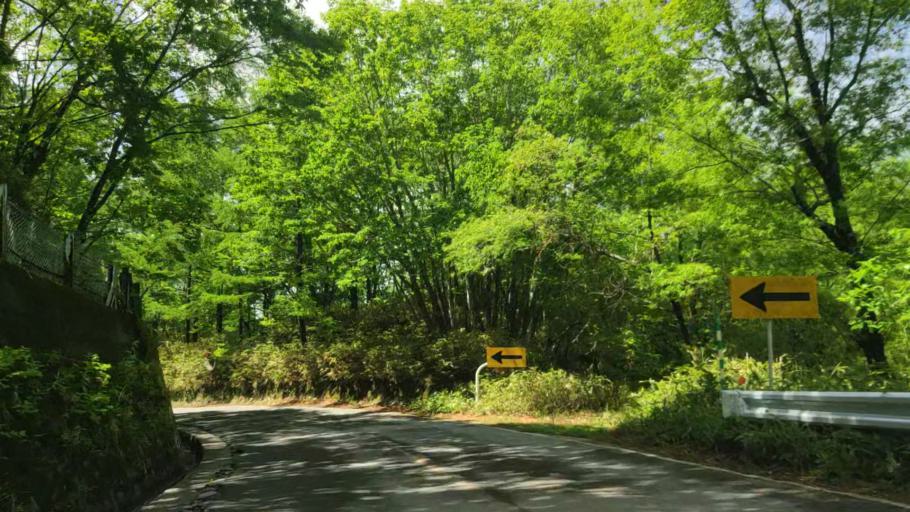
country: JP
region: Nagano
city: Chino
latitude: 36.0810
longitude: 138.2916
